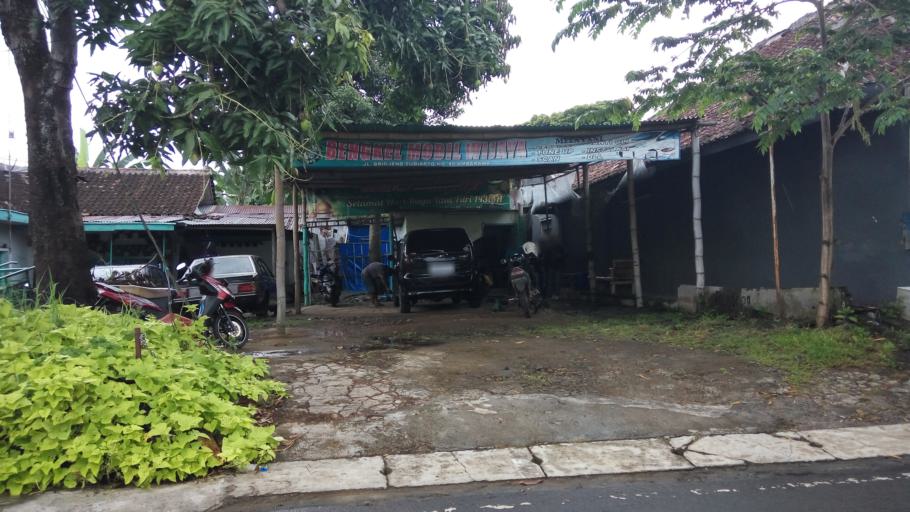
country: ID
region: Central Java
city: Ambarawa
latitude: -7.2645
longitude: 110.4063
